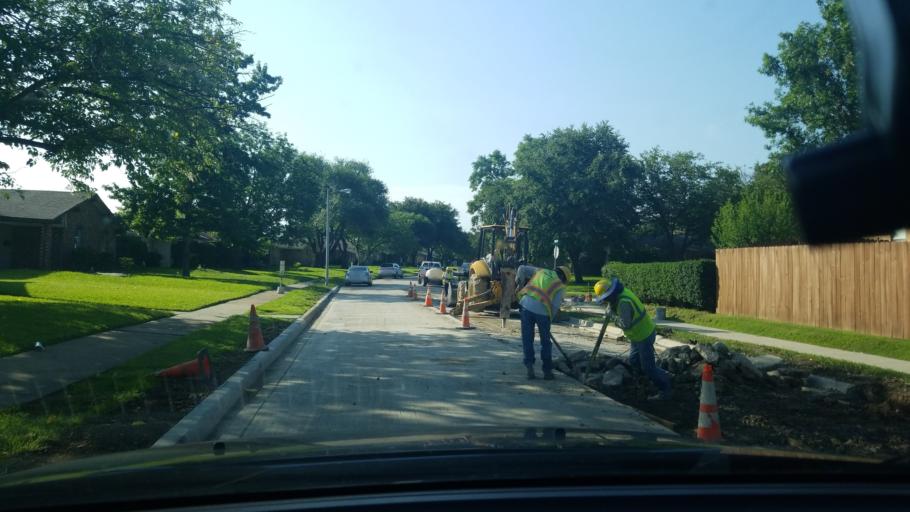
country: US
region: Texas
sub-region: Dallas County
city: Mesquite
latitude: 32.8189
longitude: -96.6457
